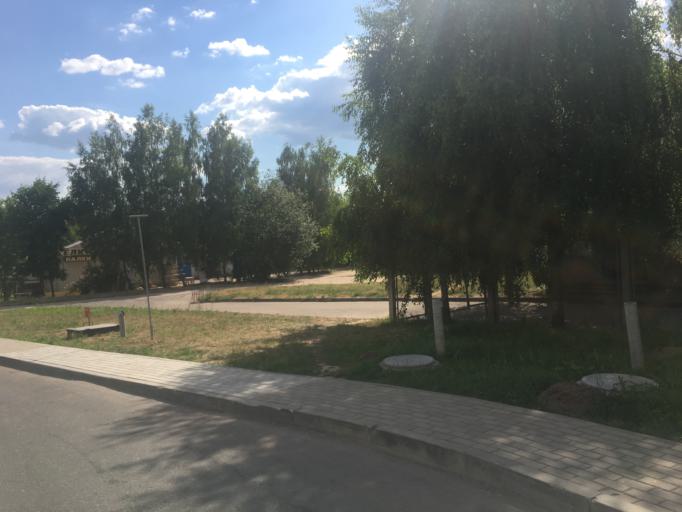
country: BY
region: Grodnenskaya
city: Hrodna
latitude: 53.6642
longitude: 23.8588
